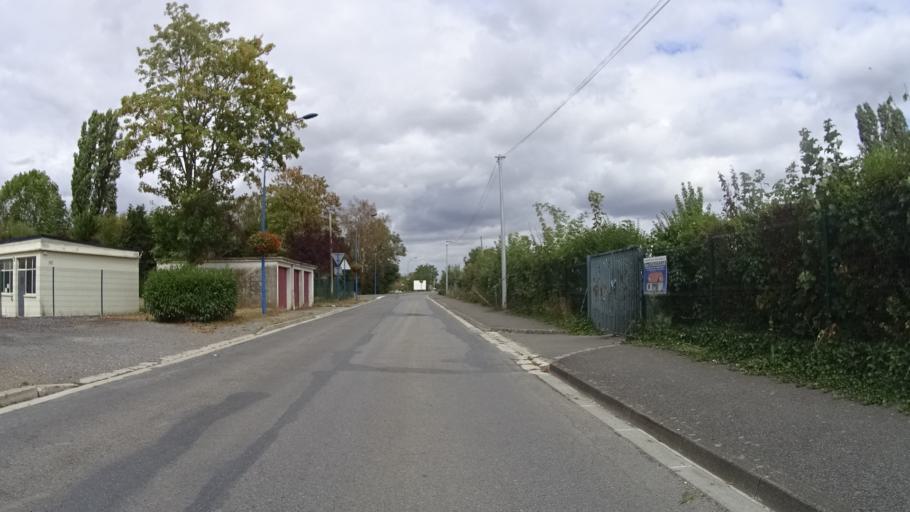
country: FR
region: Picardie
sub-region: Departement de l'Aisne
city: Beautor
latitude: 49.6500
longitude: 3.3388
